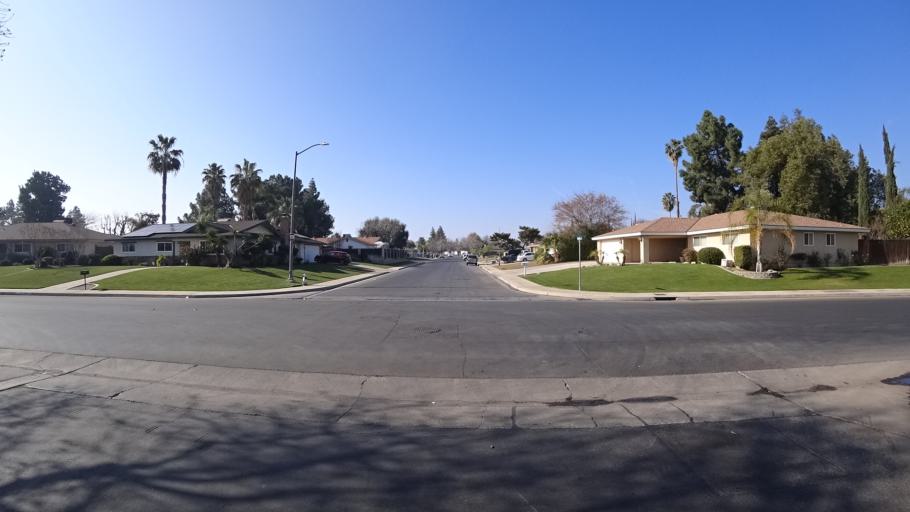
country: US
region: California
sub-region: Kern County
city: Bakersfield
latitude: 35.3334
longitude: -119.0603
